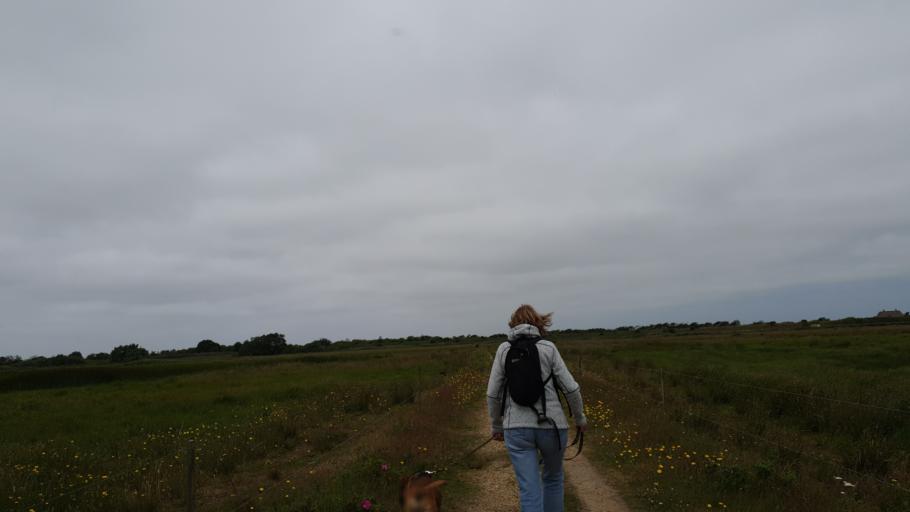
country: DK
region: Central Jutland
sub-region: Ringkobing-Skjern Kommune
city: Skjern
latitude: 55.9152
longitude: 8.4065
